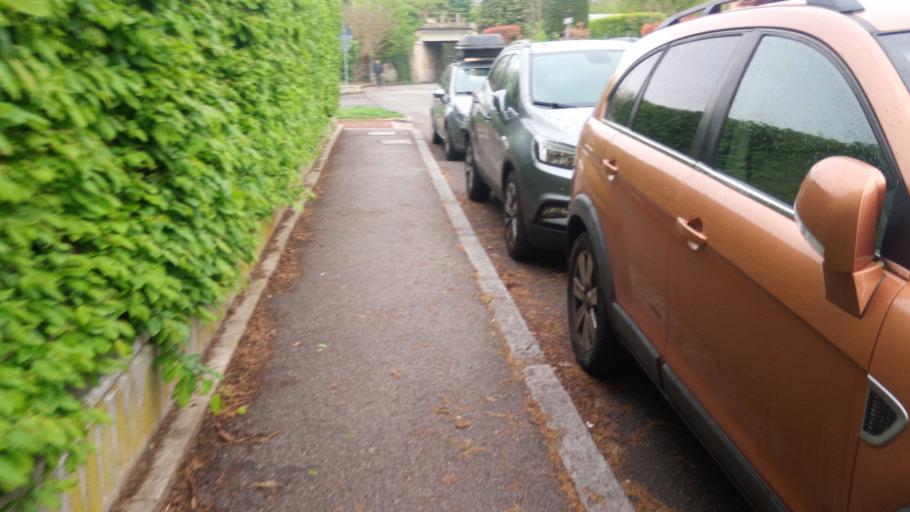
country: IT
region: Emilia-Romagna
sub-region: Provincia di Bologna
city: Bologna
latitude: 44.5209
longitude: 11.3400
